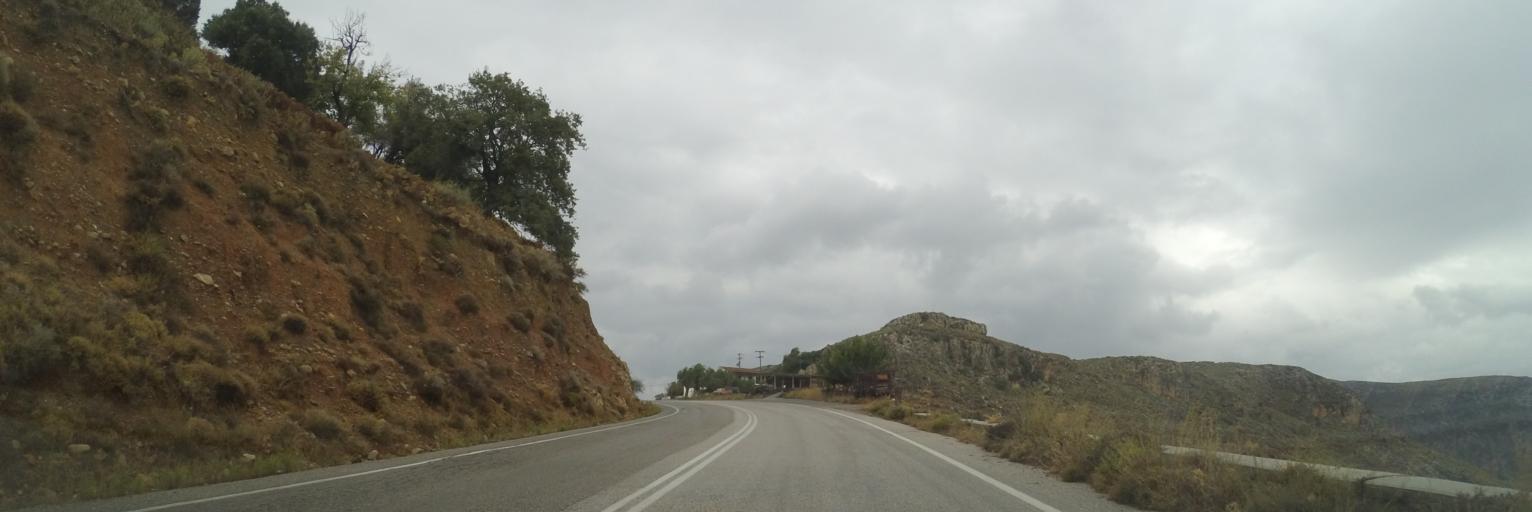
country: GR
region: Crete
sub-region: Nomos Rethymnis
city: Agia Foteini
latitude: 35.2942
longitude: 24.5648
